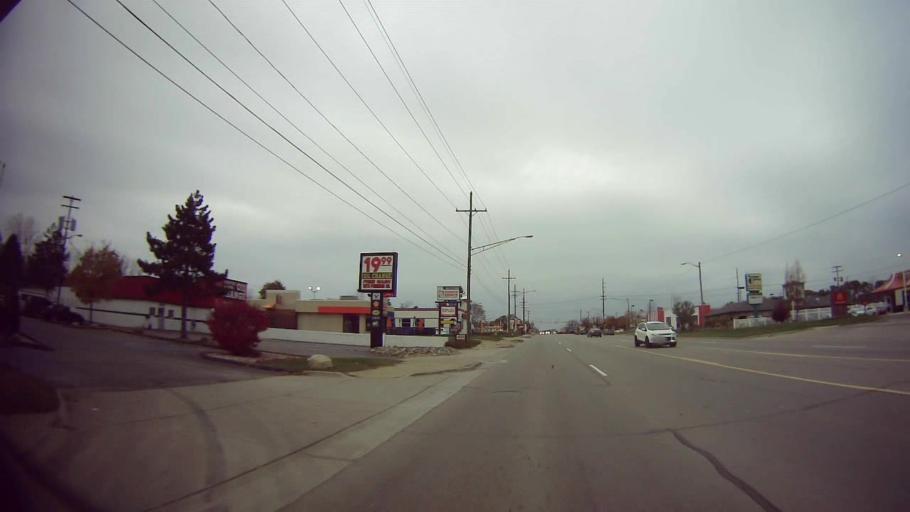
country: US
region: Michigan
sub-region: Oakland County
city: Waterford
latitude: 42.6882
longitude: -83.3834
